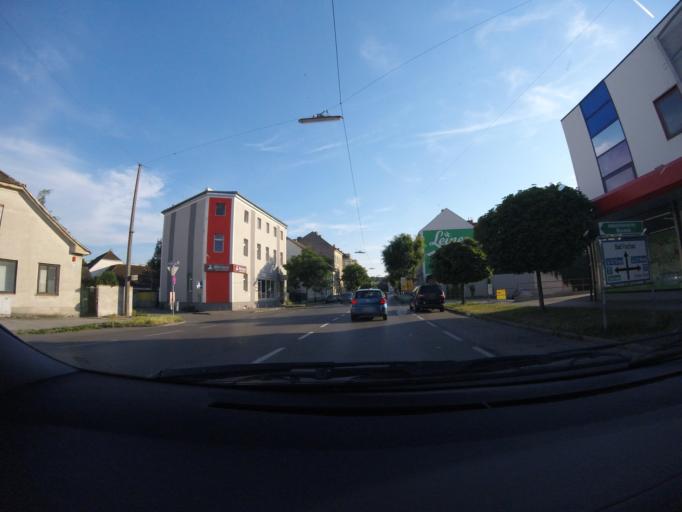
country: AT
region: Lower Austria
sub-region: Wiener Neustadt Stadt
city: Wiener Neustadt
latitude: 47.8239
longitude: 16.2490
